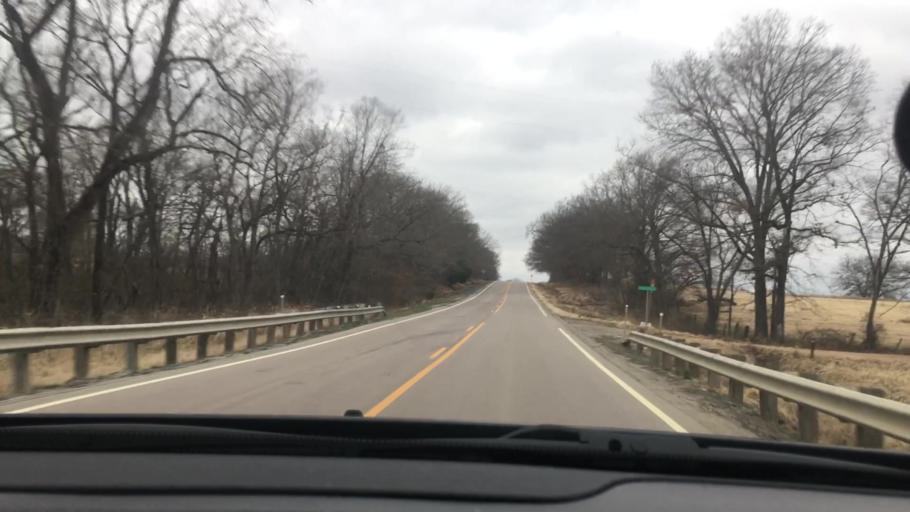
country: US
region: Oklahoma
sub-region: Coal County
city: Coalgate
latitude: 34.3722
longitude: -96.3549
